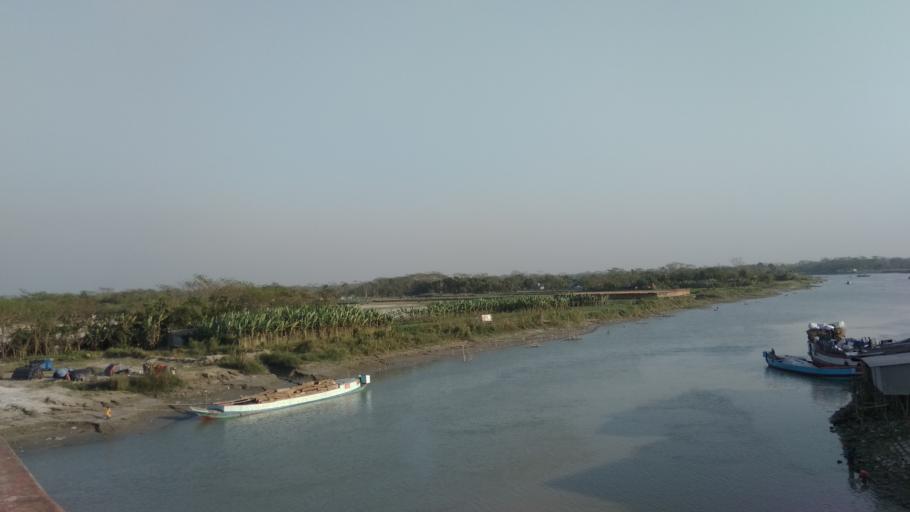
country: BD
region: Barisal
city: Mehendiganj
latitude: 22.9155
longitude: 90.4169
